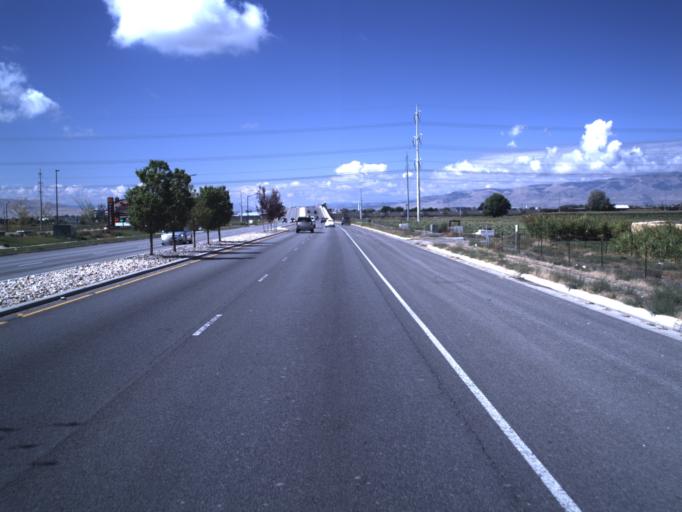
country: US
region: Utah
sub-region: Utah County
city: Springville
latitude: 40.1613
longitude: -111.6292
